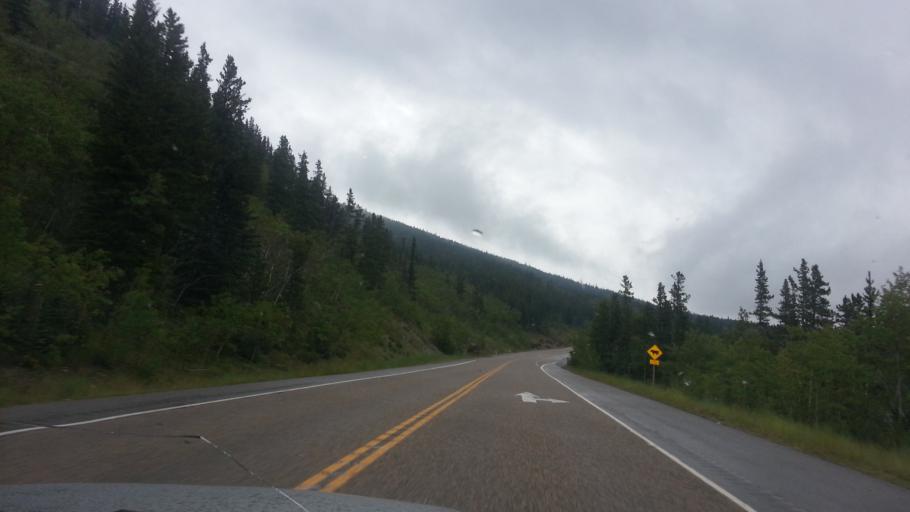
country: CA
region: Alberta
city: Cochrane
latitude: 50.8670
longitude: -114.7874
